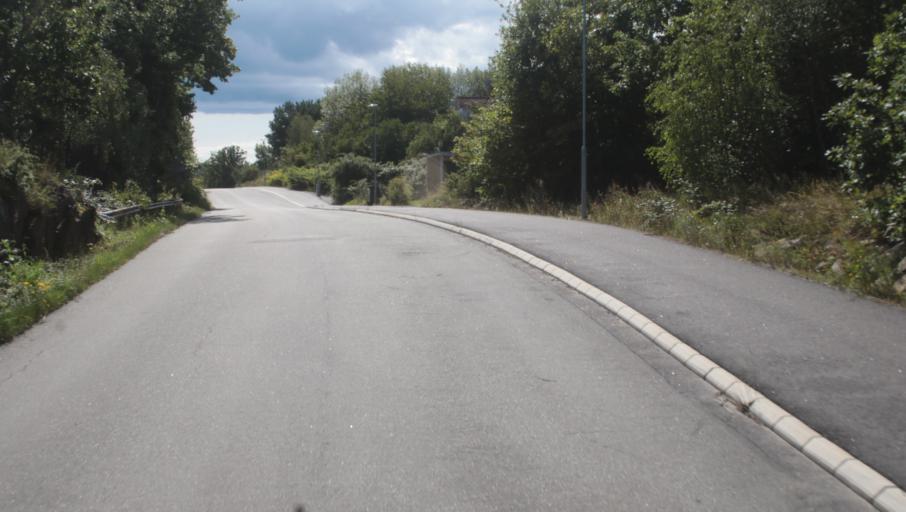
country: SE
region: Blekinge
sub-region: Karlshamns Kommun
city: Karlshamn
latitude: 56.1514
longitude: 14.8513
